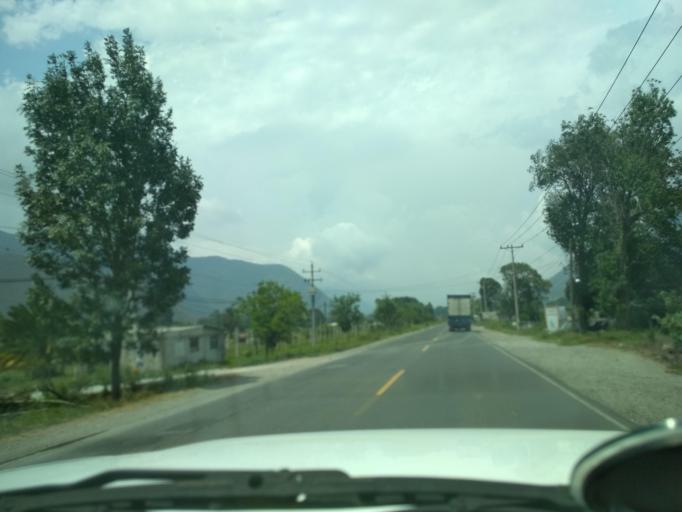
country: MX
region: Veracruz
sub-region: Nogales
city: Taza de Agua Ojo Zarco
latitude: 18.7713
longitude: -97.2165
